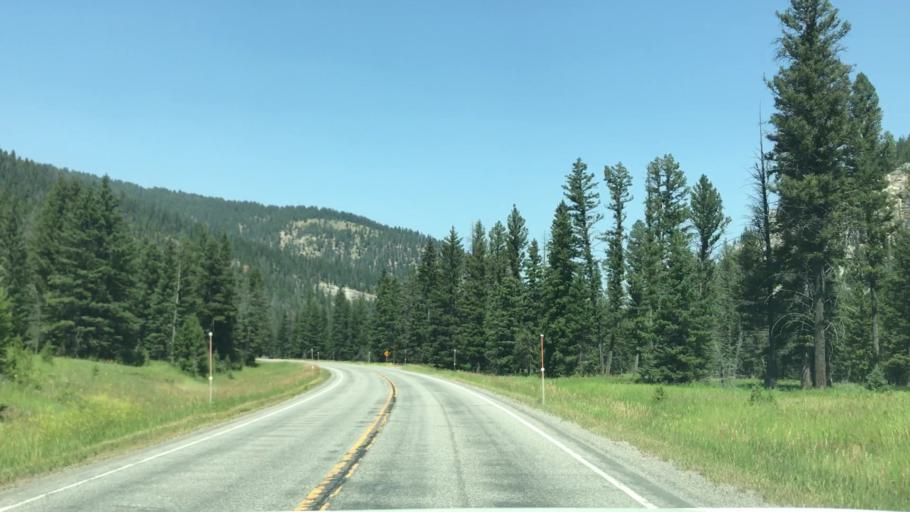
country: US
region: Montana
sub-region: Gallatin County
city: Big Sky
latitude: 45.1552
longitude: -111.2458
